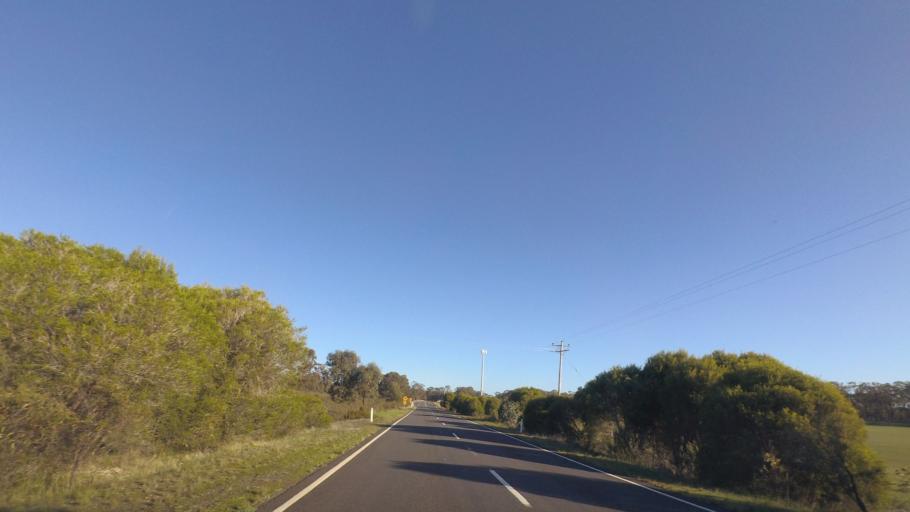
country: AU
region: Victoria
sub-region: Greater Bendigo
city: Kennington
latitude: -36.8694
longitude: 144.4997
